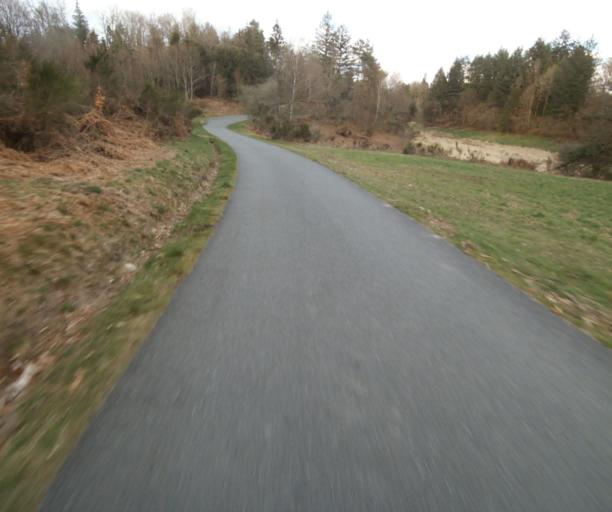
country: FR
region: Limousin
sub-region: Departement de la Correze
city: Argentat
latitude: 45.2458
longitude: 1.9554
